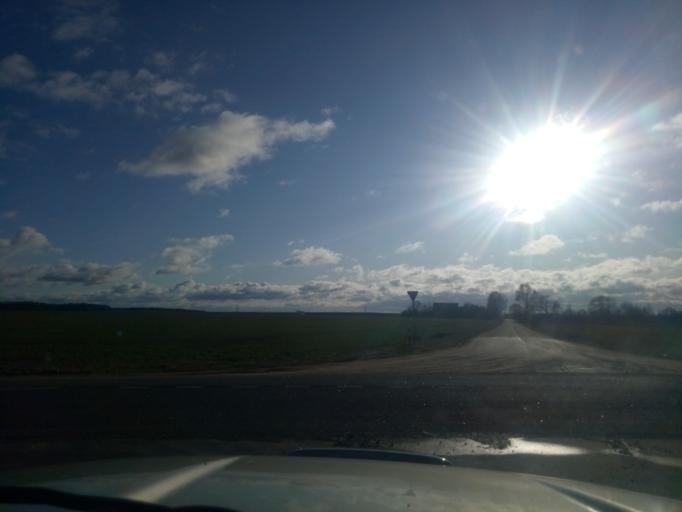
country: BY
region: Minsk
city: Tsimkavichy
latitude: 53.1328
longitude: 26.9789
